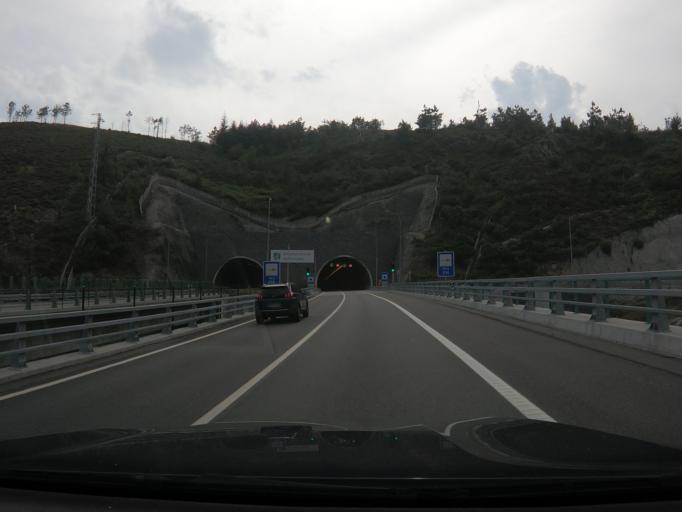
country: PT
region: Vila Real
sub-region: Santa Marta de Penaguiao
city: Santa Marta de Penaguiao
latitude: 41.2795
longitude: -7.8684
